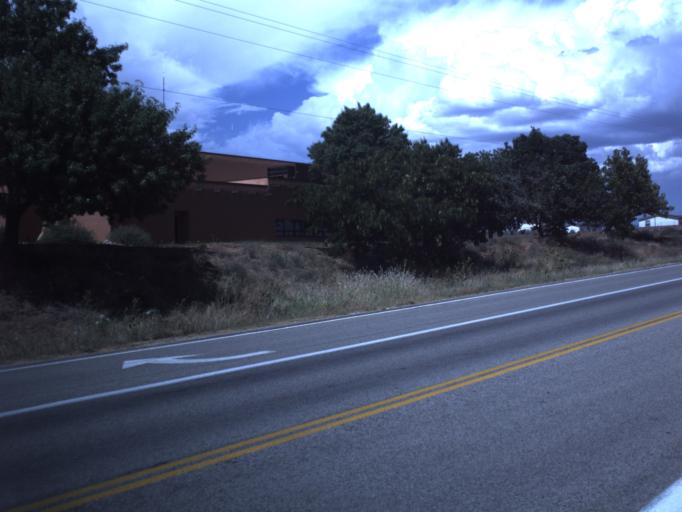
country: US
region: Utah
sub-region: San Juan County
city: Blanding
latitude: 37.5812
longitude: -109.4781
